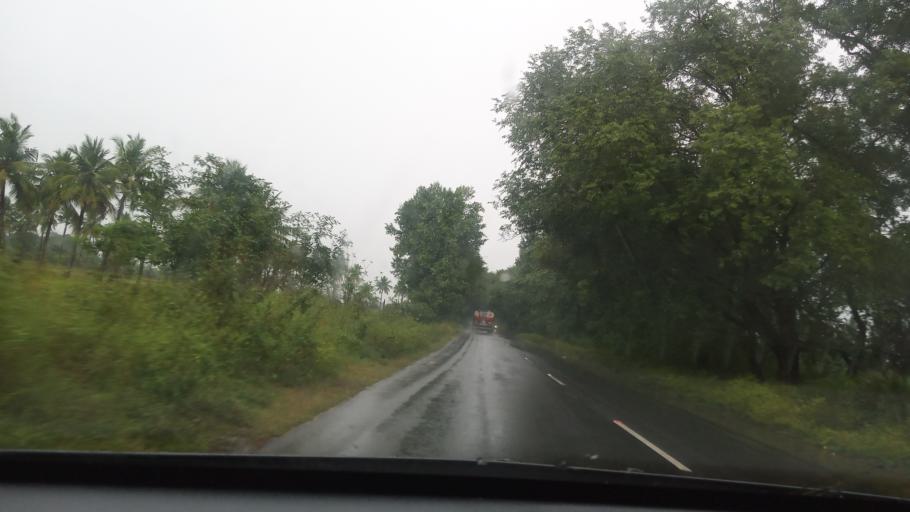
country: IN
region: Tamil Nadu
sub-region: Vellore
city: Kalavai
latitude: 12.8137
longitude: 79.4122
